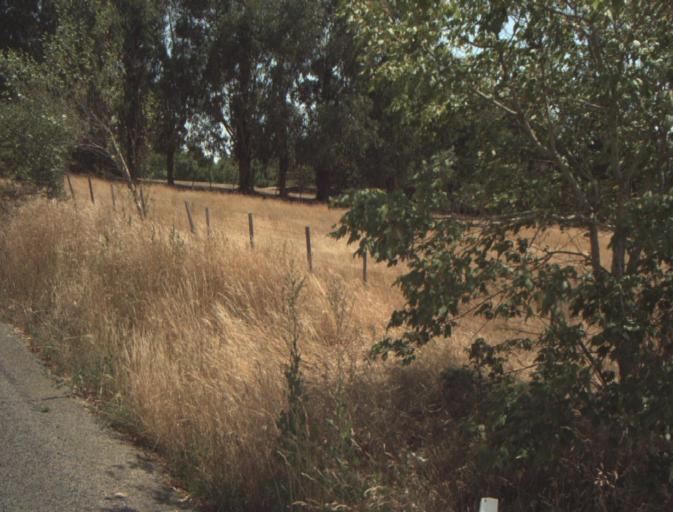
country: AU
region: Tasmania
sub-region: Launceston
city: Newstead
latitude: -41.4701
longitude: 147.1914
